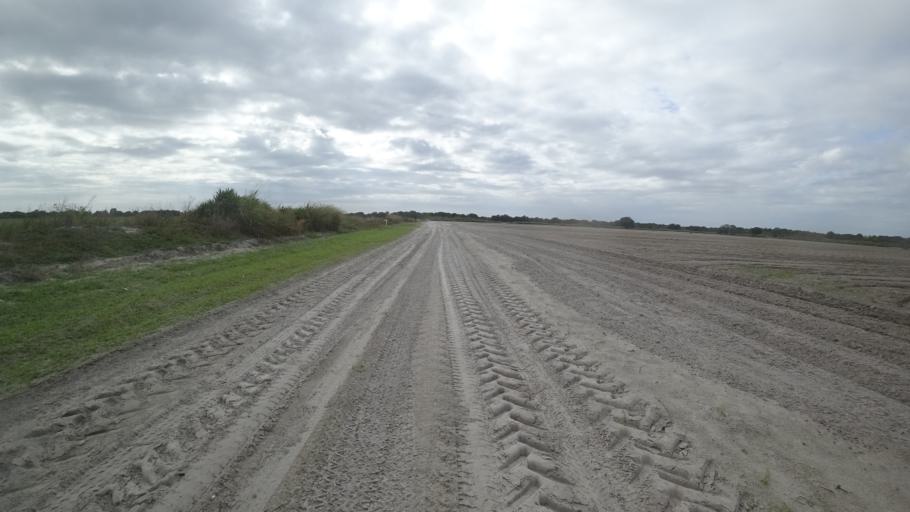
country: US
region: Florida
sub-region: Hillsborough County
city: Wimauma
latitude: 27.5620
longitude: -82.2945
